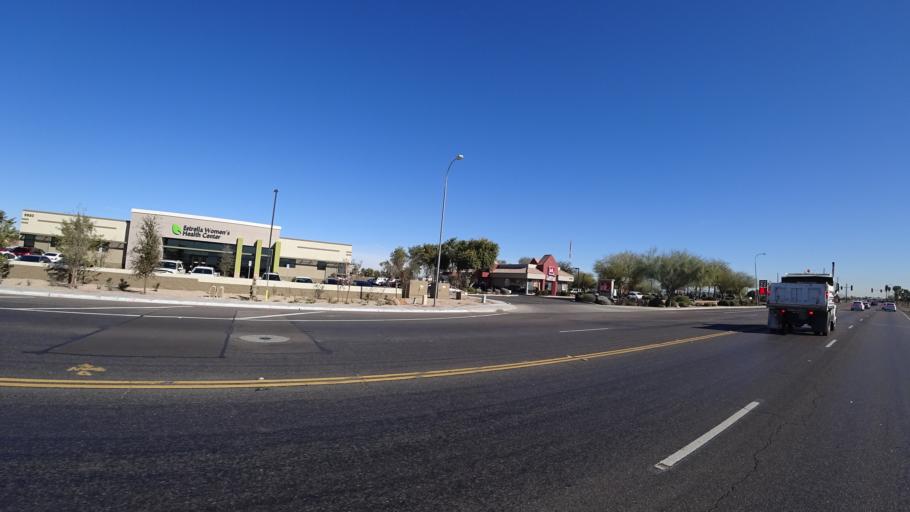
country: US
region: Arizona
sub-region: Maricopa County
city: Tolleson
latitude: 33.4937
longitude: -112.2748
